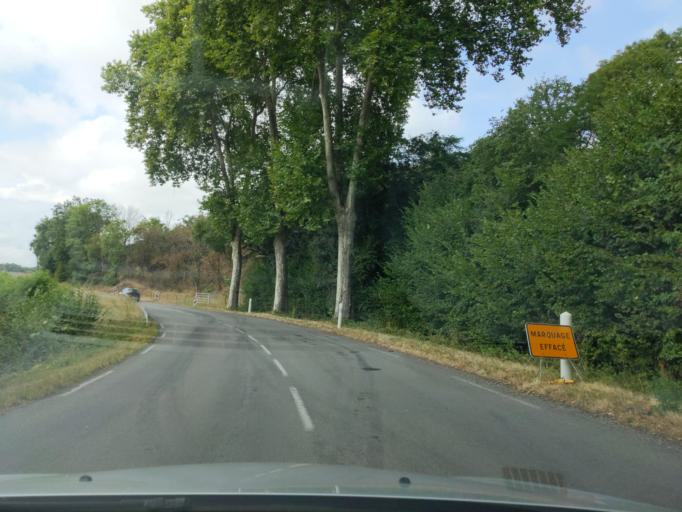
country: FR
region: Bourgogne
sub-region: Departement de Saone-et-Loire
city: Bourbon-Lancy
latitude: 46.6895
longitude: 3.8433
